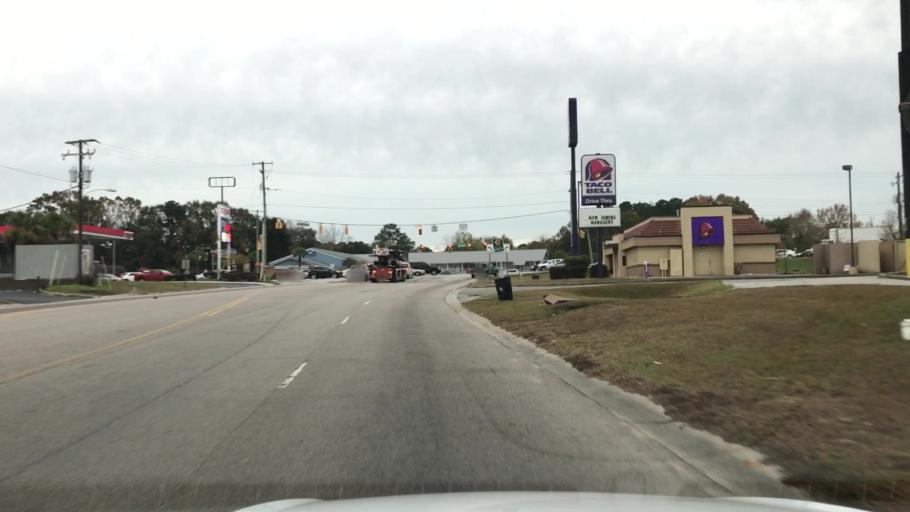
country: US
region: South Carolina
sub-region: Berkeley County
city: Hanahan
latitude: 32.9364
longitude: -80.0455
